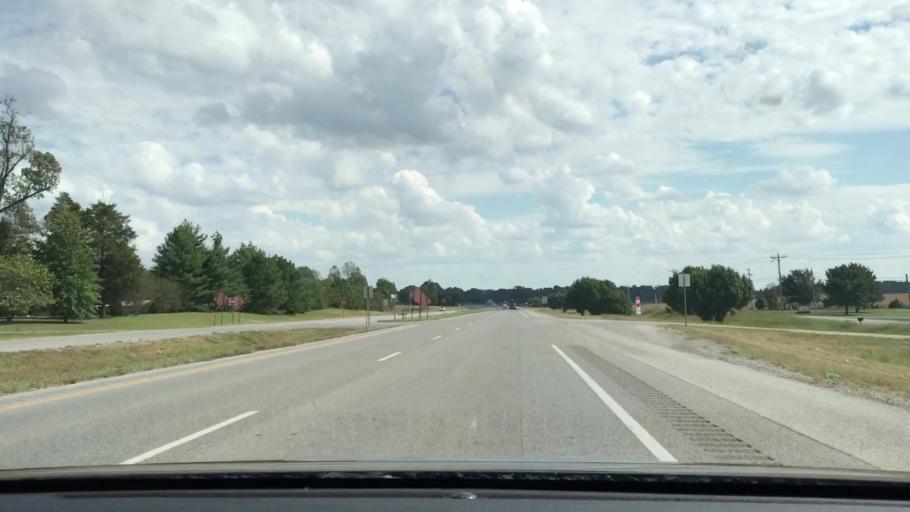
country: US
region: Kentucky
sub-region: Trigg County
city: Cadiz
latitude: 36.8676
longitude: -87.7888
